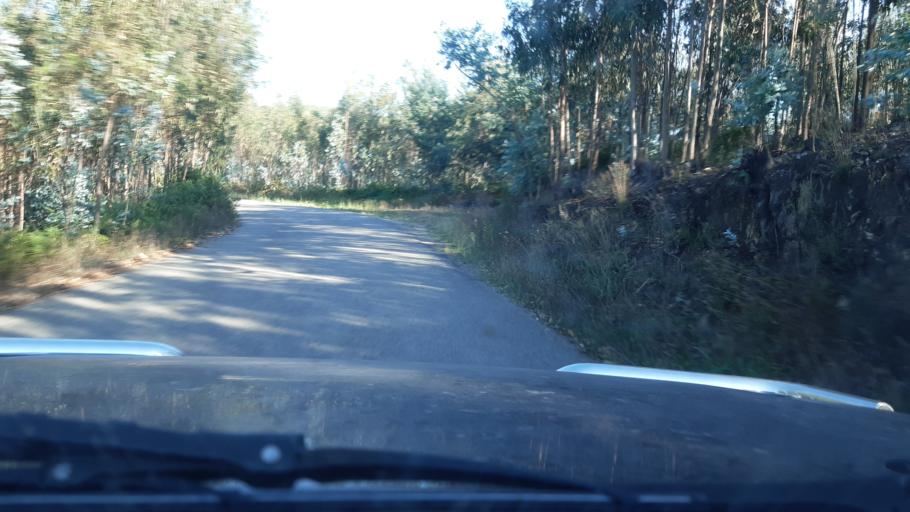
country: PT
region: Aveiro
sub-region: Agueda
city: Aguada de Cima
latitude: 40.5680
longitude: -8.3243
